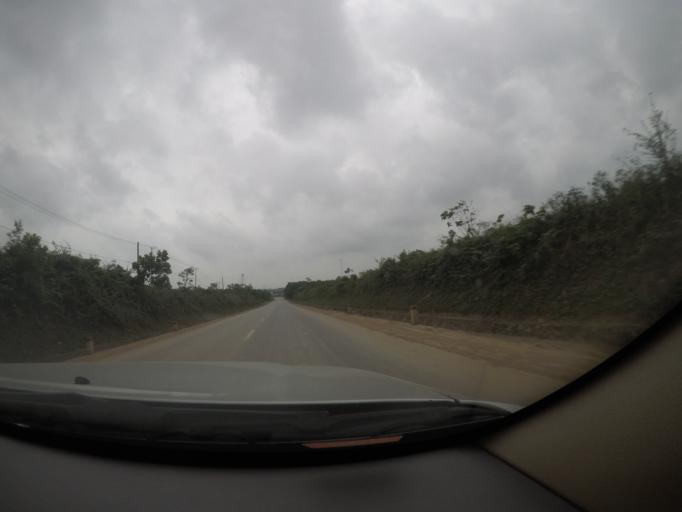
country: VN
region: Quang Tri
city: Dong Ha
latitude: 16.7909
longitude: 107.0565
